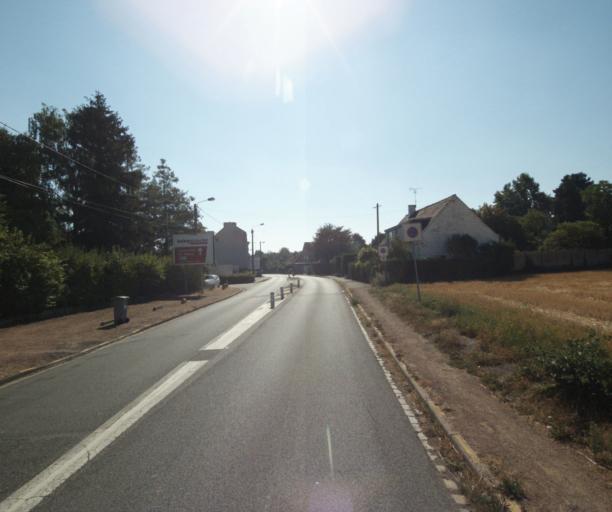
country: FR
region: Nord-Pas-de-Calais
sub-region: Departement du Nord
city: Wervicq-Sud
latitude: 50.7735
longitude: 3.0619
